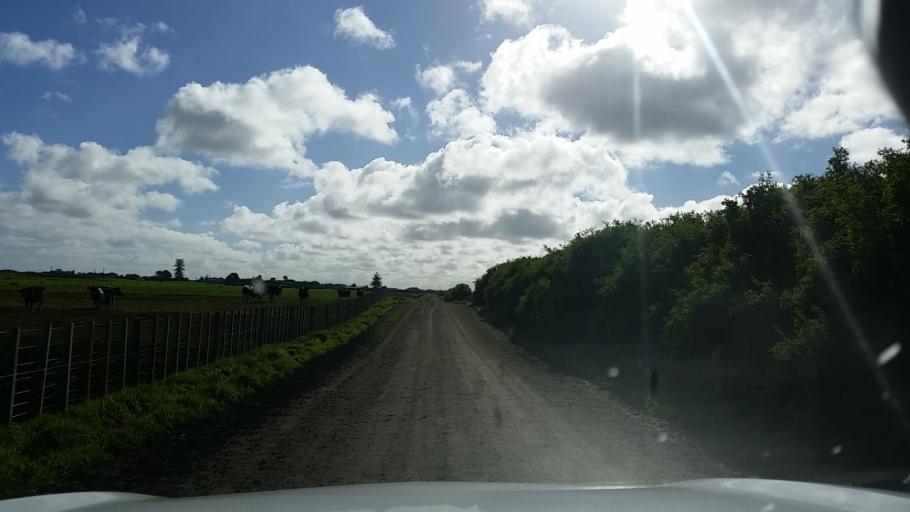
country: NZ
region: Taranaki
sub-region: South Taranaki District
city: Patea
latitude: -39.7543
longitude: 174.5221
